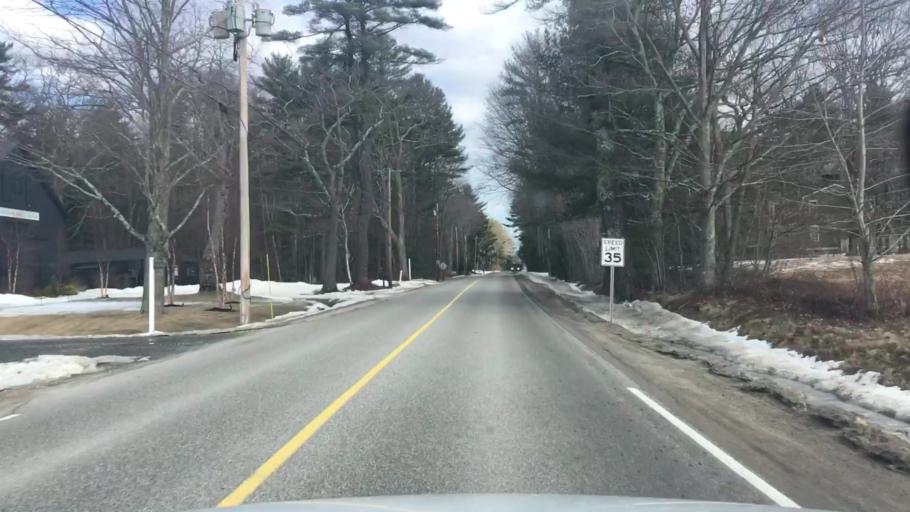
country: US
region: Maine
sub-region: York County
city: Kennebunk
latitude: 43.4050
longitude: -70.5210
